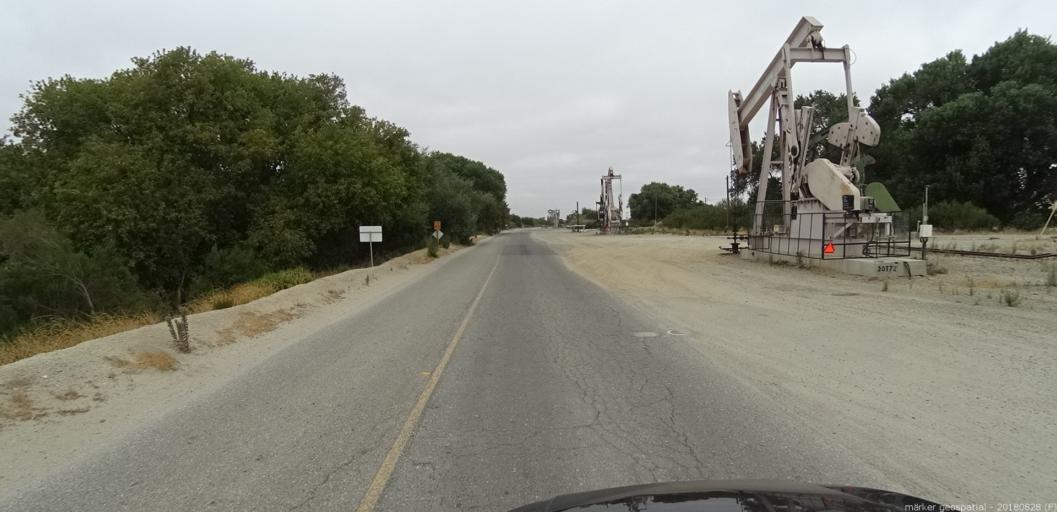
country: US
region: California
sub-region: San Luis Obispo County
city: Lake Nacimiento
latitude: 35.9575
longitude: -120.8773
